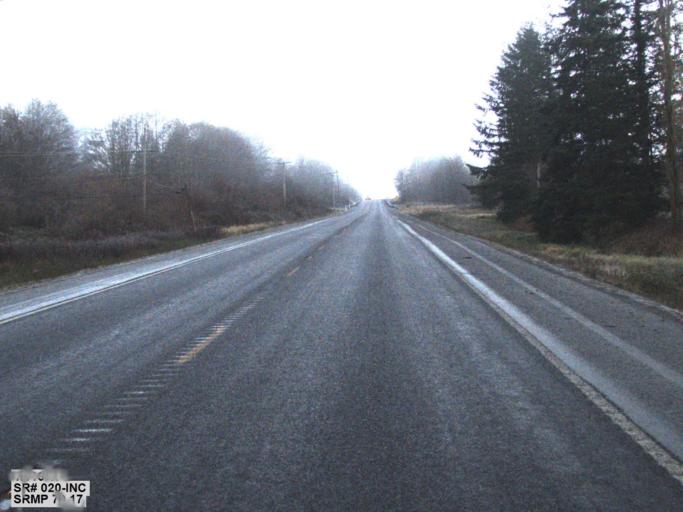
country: US
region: Washington
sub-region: Skagit County
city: Sedro-Woolley
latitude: 48.5235
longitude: -121.9543
